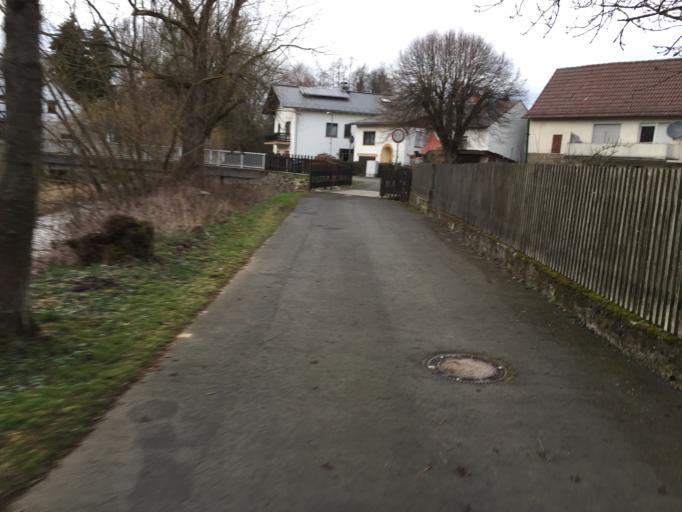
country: DE
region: Hesse
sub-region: Regierungsbezirk Giessen
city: Rabenau
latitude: 50.6694
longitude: 8.8717
